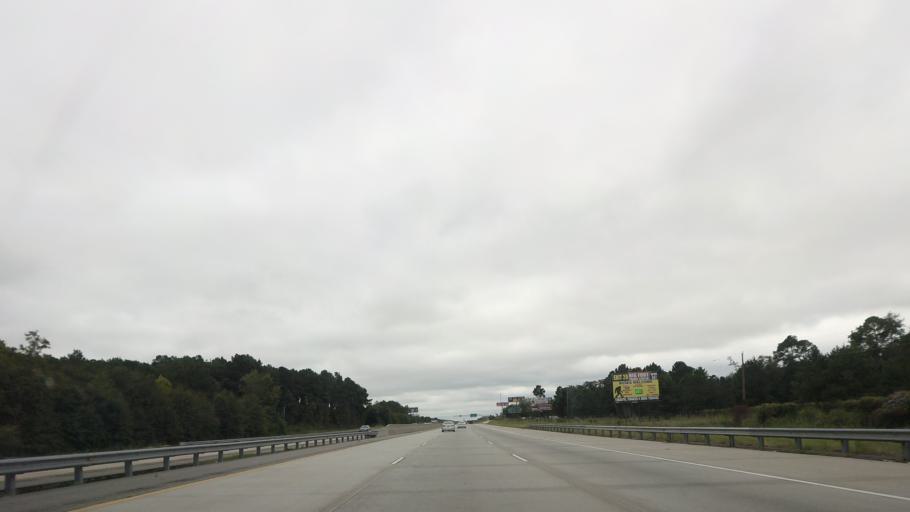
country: US
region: Georgia
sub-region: Lowndes County
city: Hahira
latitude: 31.0515
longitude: -83.3972
